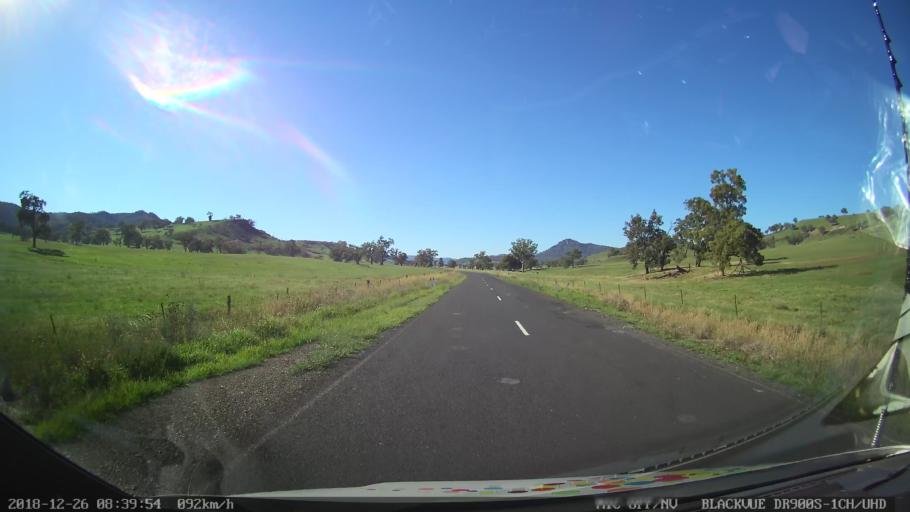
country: AU
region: New South Wales
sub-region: Mid-Western Regional
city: Kandos
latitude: -32.4597
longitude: 150.0756
